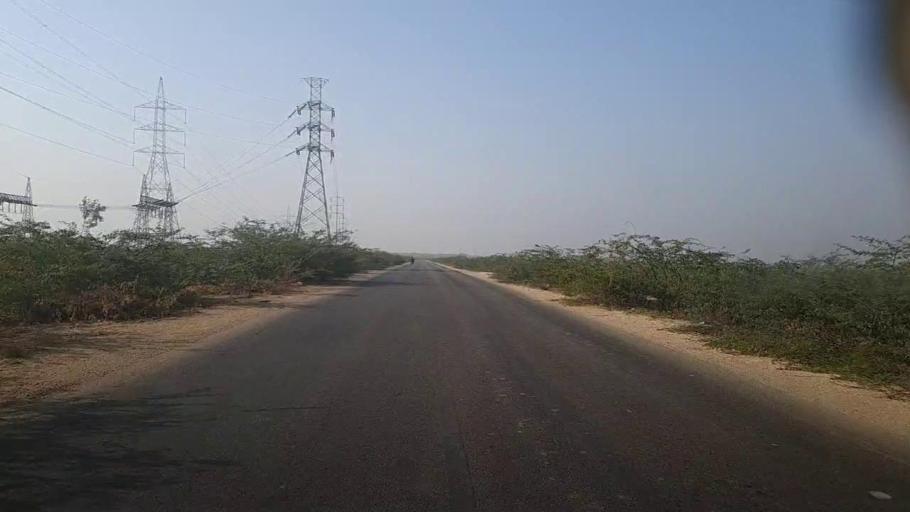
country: PK
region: Sindh
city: Gharo
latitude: 24.7616
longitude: 67.5440
